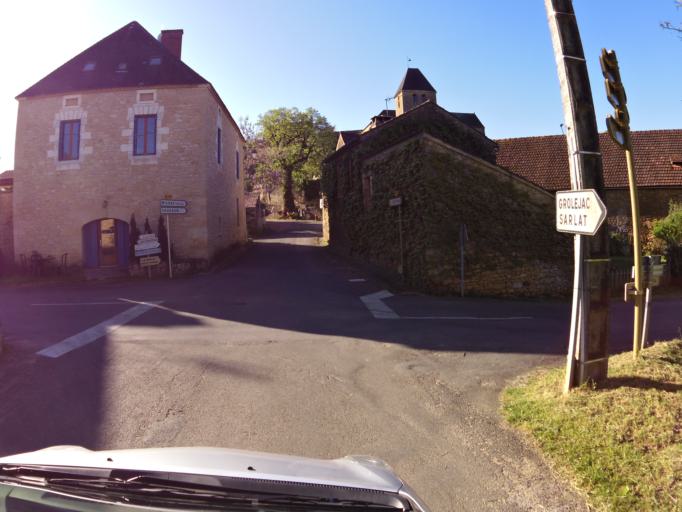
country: FR
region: Midi-Pyrenees
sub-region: Departement du Lot
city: Gourdon
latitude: 44.7991
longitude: 1.3471
